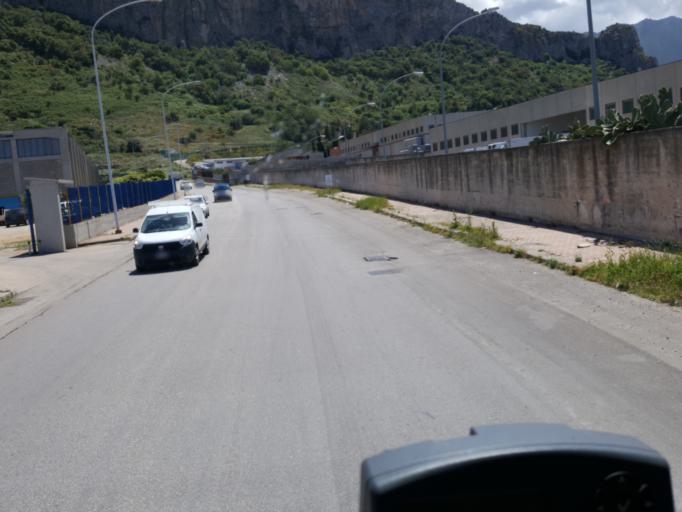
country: IT
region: Sicily
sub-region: Palermo
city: Carini
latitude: 38.1517
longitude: 13.2067
